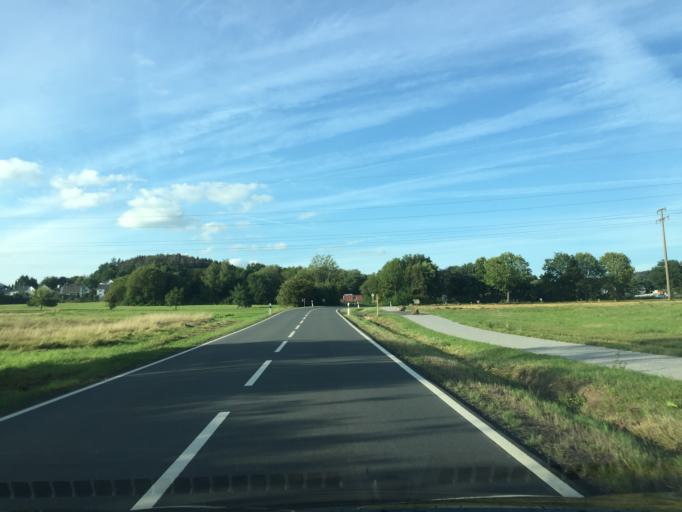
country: DE
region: Rheinland-Pfalz
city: Heiligenroth
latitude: 50.4577
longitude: 7.8709
